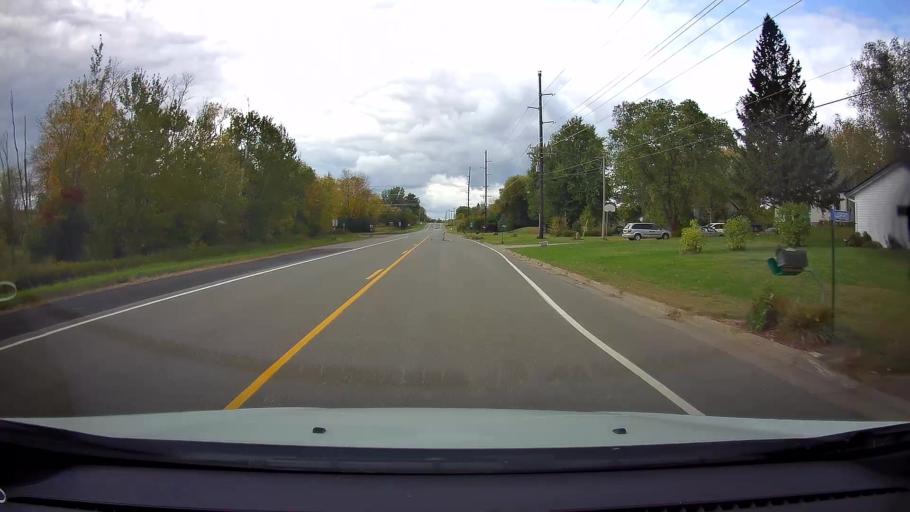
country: US
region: Minnesota
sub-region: Chisago County
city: Center City
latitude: 45.3973
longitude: -92.8037
